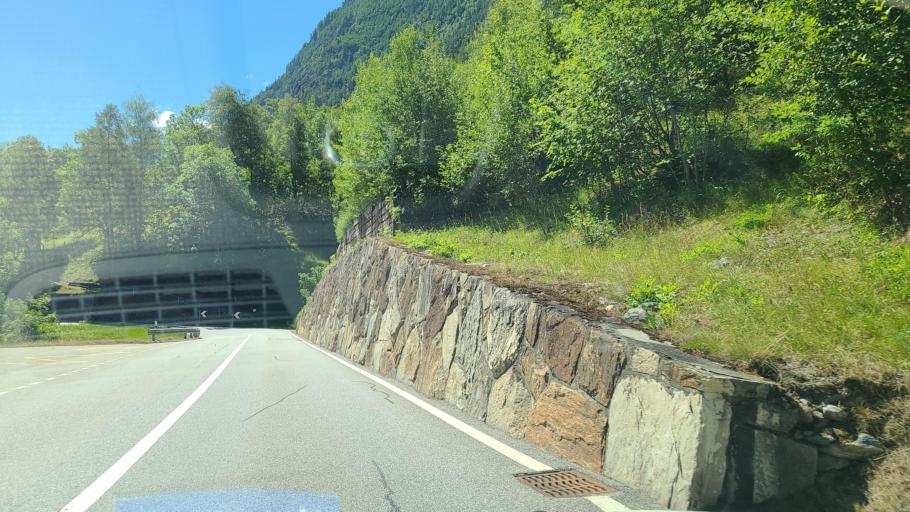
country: CH
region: Valais
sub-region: Visp District
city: Stalden
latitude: 46.2241
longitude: 7.8742
